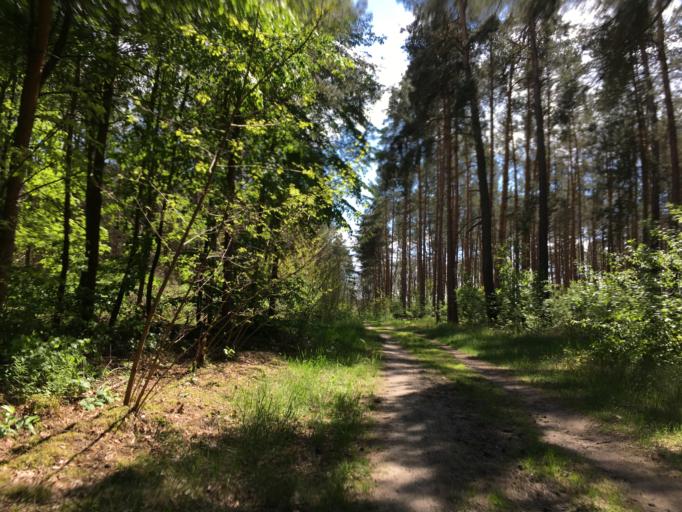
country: DE
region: Brandenburg
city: Rudnitz
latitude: 52.7177
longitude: 13.6574
